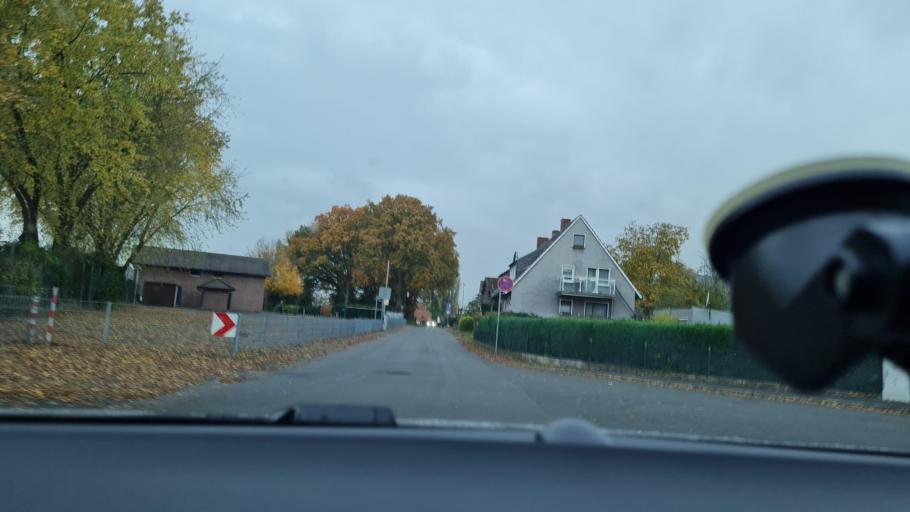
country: DE
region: North Rhine-Westphalia
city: Rheinberg
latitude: 51.6000
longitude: 6.6227
